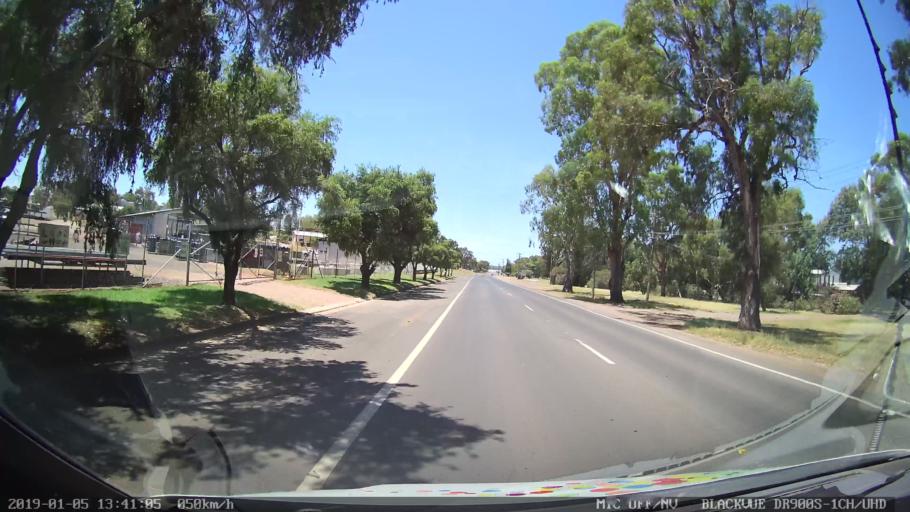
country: AU
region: New South Wales
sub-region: Gunnedah
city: Gunnedah
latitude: -30.9796
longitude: 150.2362
